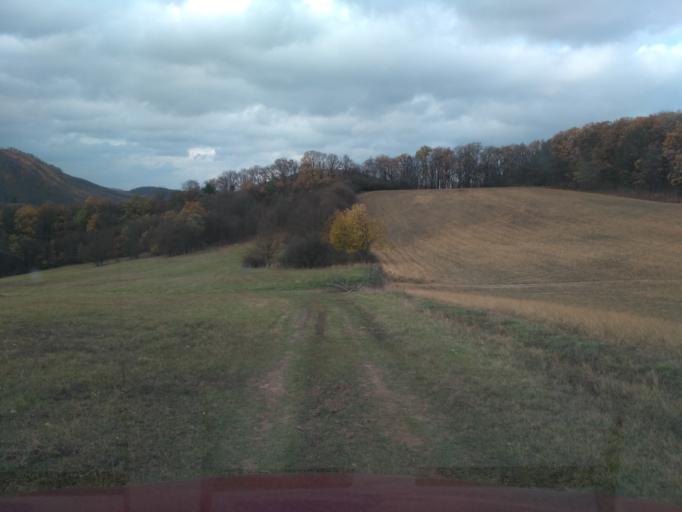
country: SK
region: Presovsky
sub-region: Okres Presov
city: Presov
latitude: 48.8737
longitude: 21.2319
